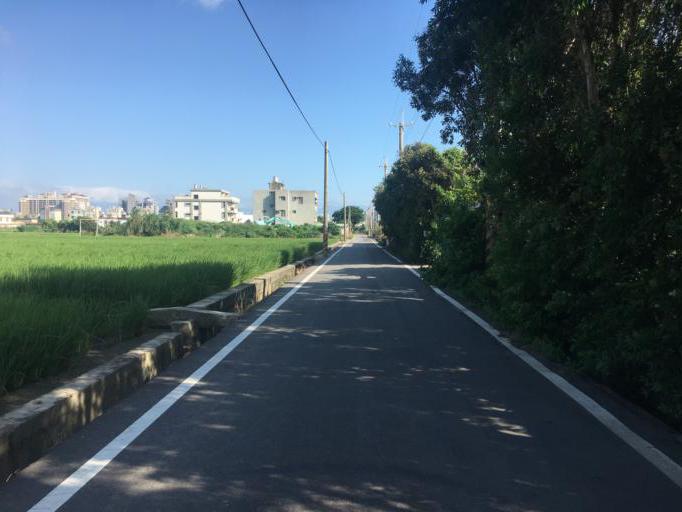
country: TW
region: Taiwan
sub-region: Hsinchu
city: Zhubei
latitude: 24.8399
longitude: 120.9883
